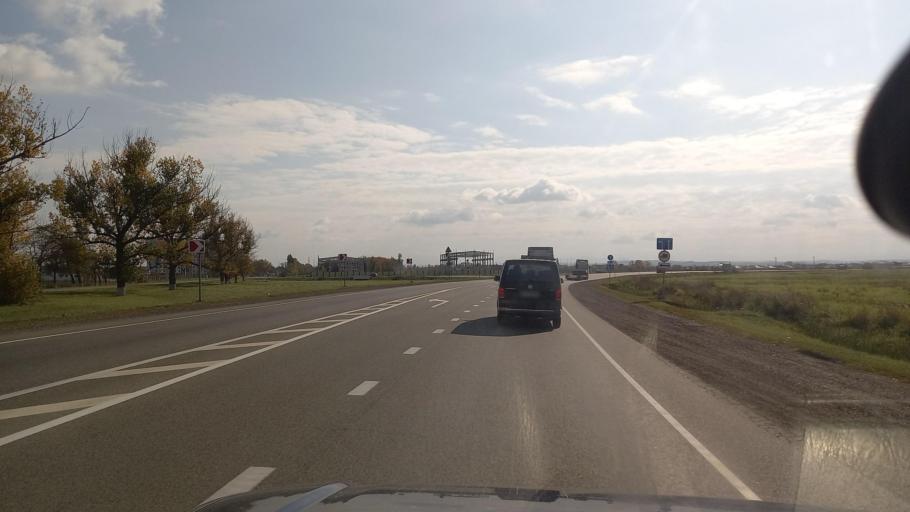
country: RU
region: Krasnodarskiy
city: Abinsk
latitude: 44.8710
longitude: 38.1273
